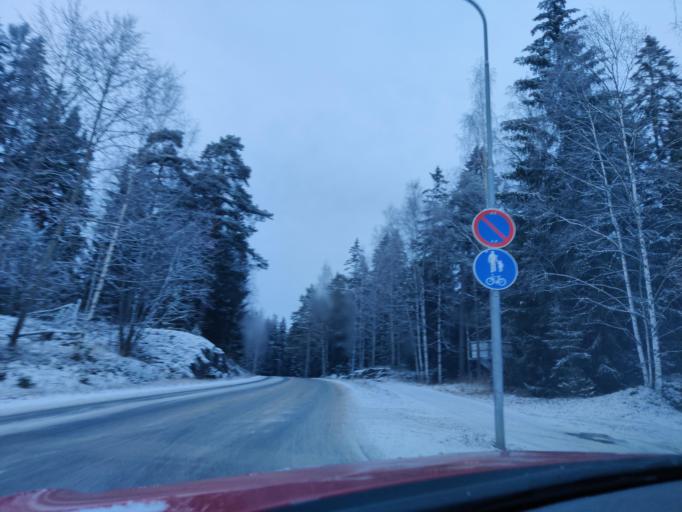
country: FI
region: Pirkanmaa
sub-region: Tampere
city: Tampere
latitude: 61.5086
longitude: 23.7944
